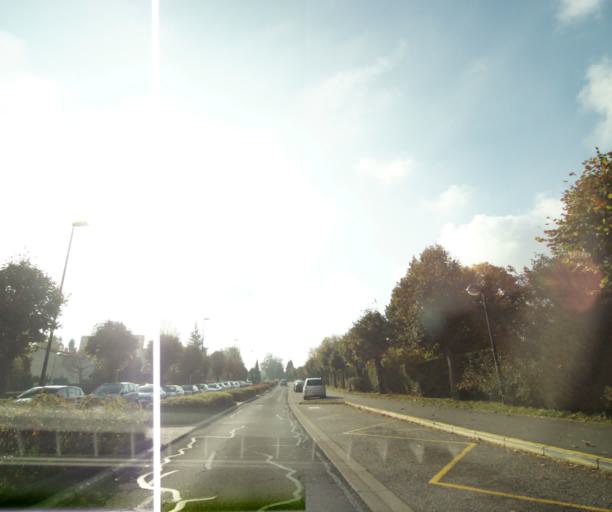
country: FR
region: Lorraine
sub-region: Departement de Meurthe-et-Moselle
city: Briey
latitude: 49.2570
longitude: 5.9351
